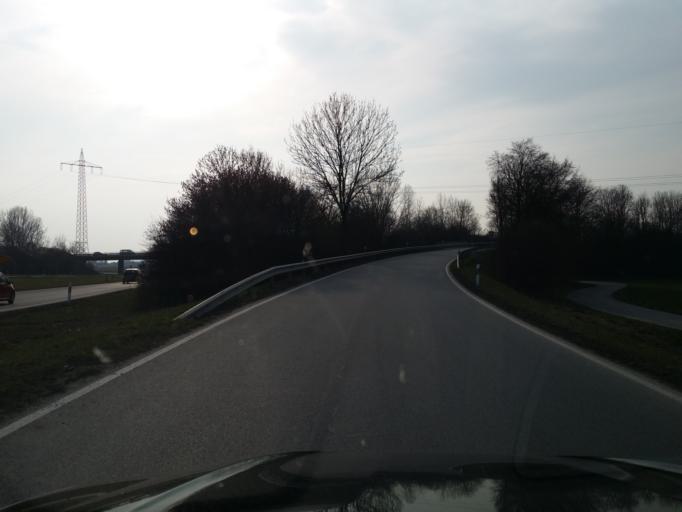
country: DE
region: Bavaria
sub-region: Lower Bavaria
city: Ergolding
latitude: 48.5788
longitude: 12.1912
